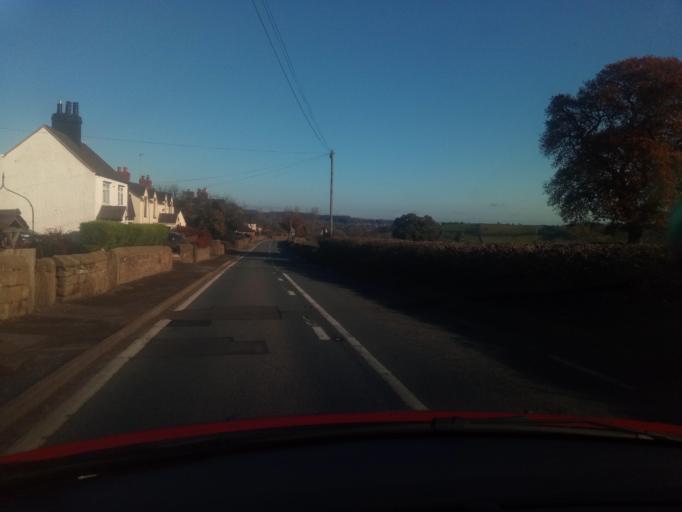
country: GB
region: England
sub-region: Derbyshire
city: Belper
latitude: 53.0216
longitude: -1.5246
